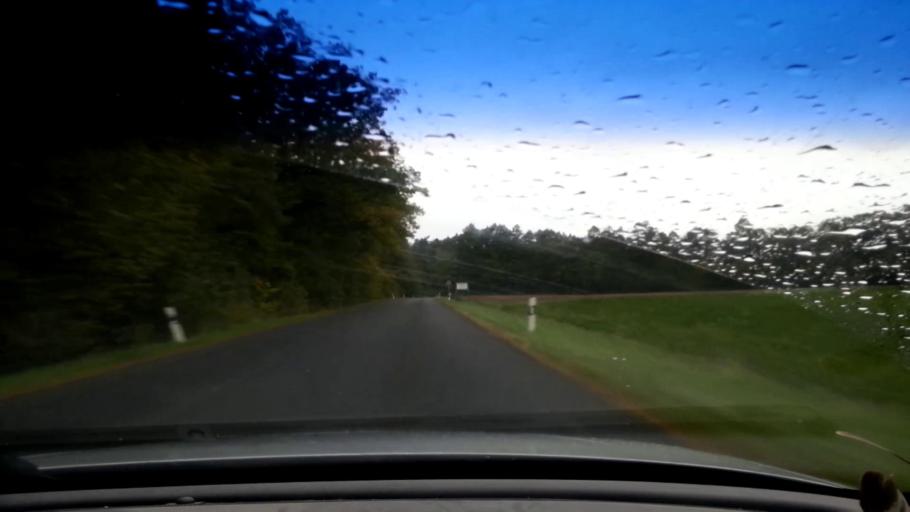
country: DE
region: Bavaria
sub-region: Upper Franconia
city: Priesendorf
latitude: 49.8667
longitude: 10.6880
